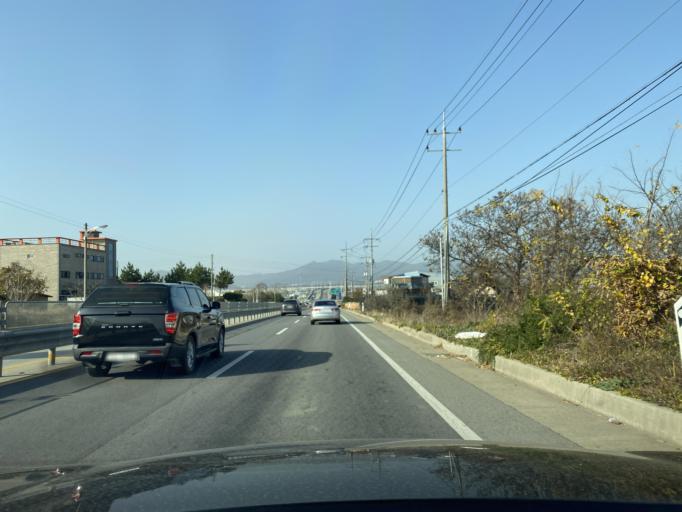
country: KR
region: Chungcheongnam-do
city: Yesan
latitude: 36.6904
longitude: 126.7466
